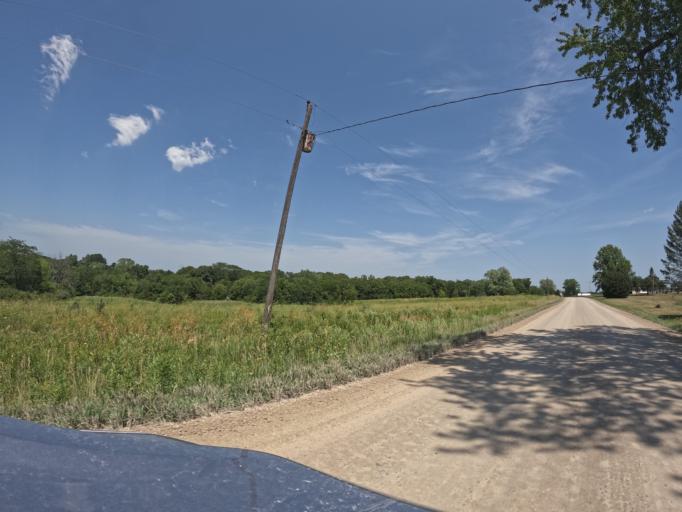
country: US
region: Iowa
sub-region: Henry County
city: Mount Pleasant
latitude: 40.9454
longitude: -91.6101
